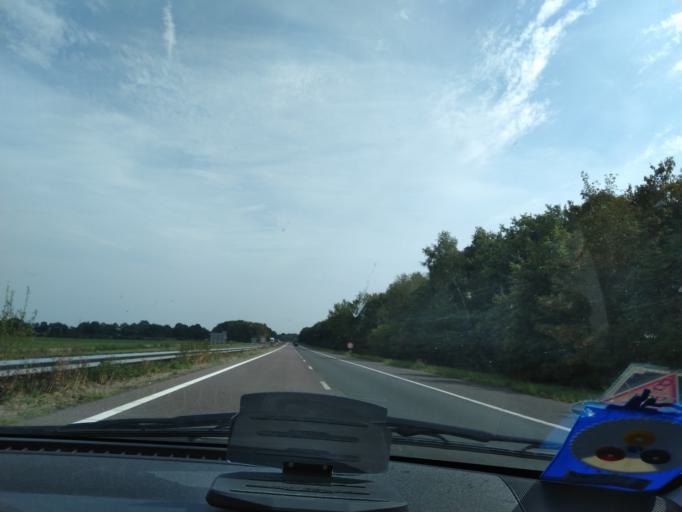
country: NL
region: Drenthe
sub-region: Gemeente Emmen
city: Klazienaveen
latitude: 52.7283
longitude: 7.0446
